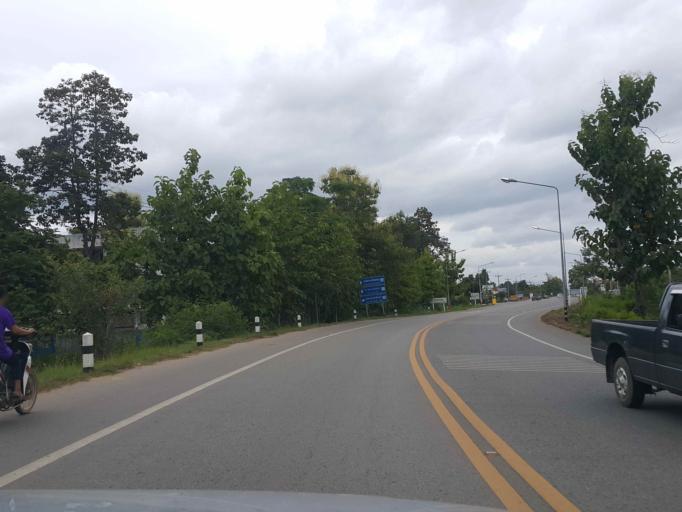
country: TH
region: Lamphun
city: Li
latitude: 17.7726
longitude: 98.9575
